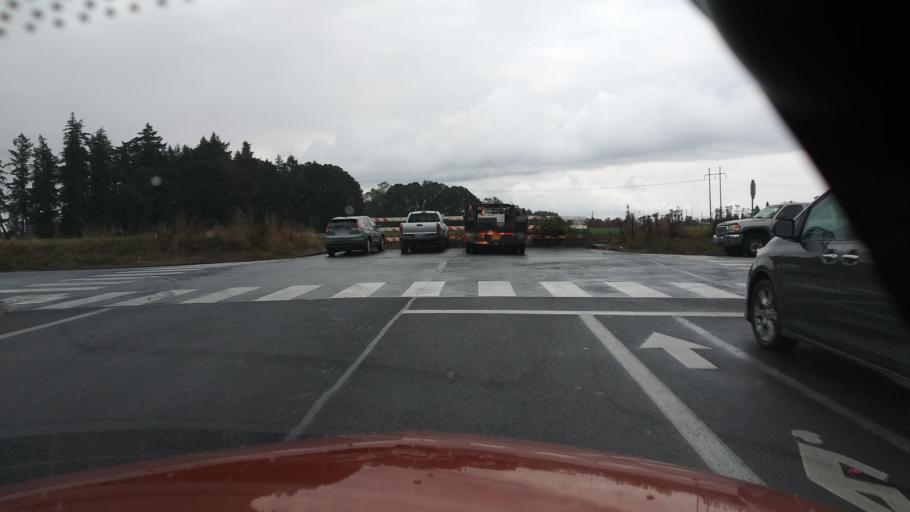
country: US
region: Oregon
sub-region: Washington County
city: Forest Grove
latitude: 45.5273
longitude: -123.0939
